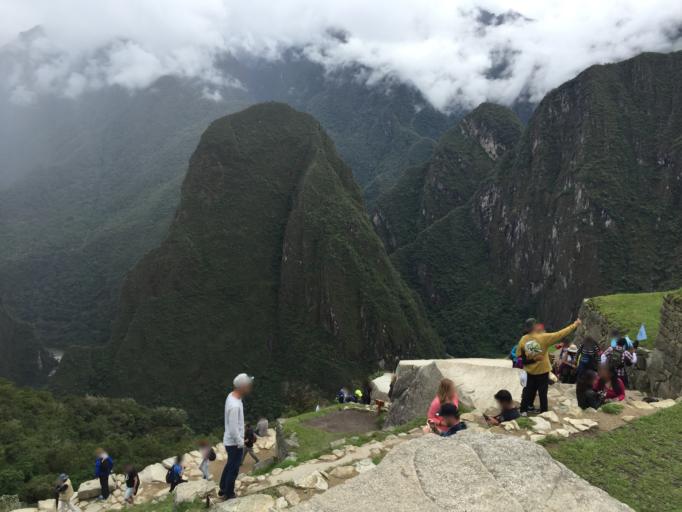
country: PE
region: Cusco
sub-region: Provincia de La Convencion
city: Santa Teresa
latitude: -13.1652
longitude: -72.5447
